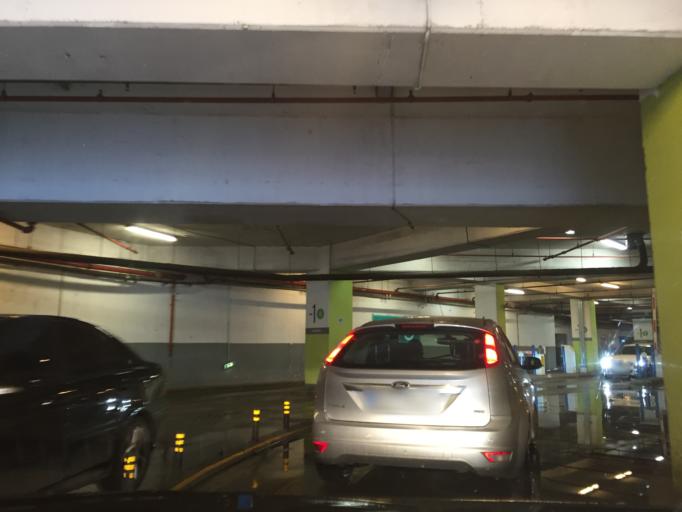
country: RO
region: Bucuresti
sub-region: Municipiul Bucuresti
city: Bucuresti
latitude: 44.4293
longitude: 26.0516
